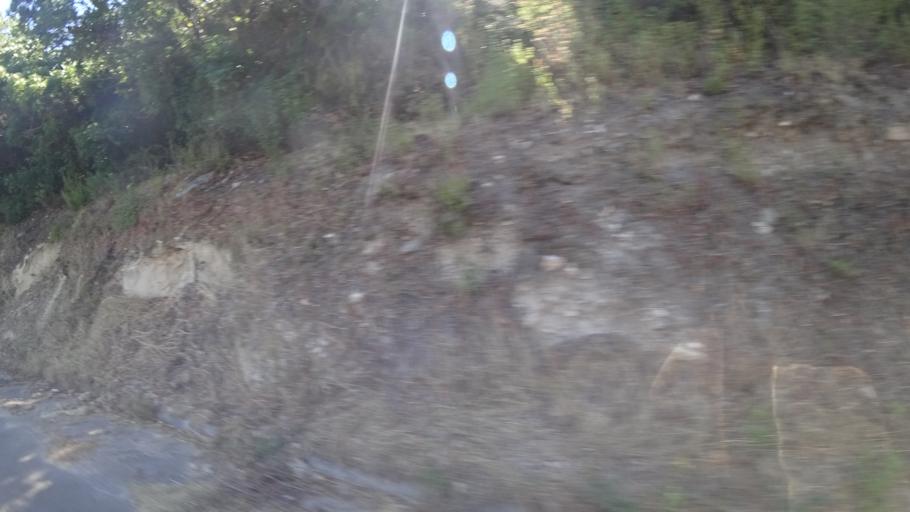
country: FR
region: Corsica
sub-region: Departement de la Corse-du-Sud
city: Alata
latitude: 41.9785
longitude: 8.6816
